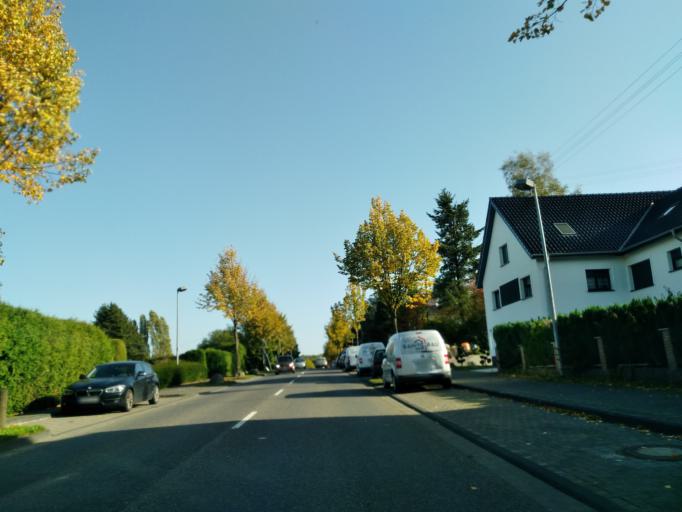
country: DE
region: North Rhine-Westphalia
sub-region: Regierungsbezirk Koln
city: Hennef
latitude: 50.7411
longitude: 7.3542
